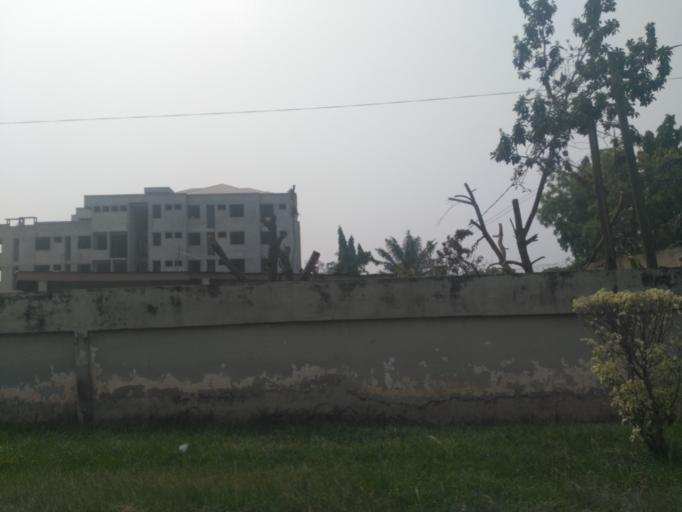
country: GH
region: Ashanti
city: Kumasi
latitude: 6.6826
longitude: -1.6335
